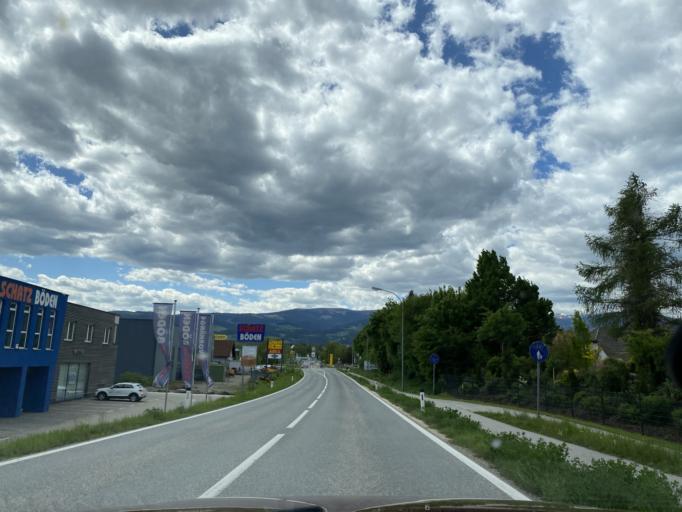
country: AT
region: Carinthia
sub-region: Politischer Bezirk Wolfsberg
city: Wolfsberg
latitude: 46.8186
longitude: 14.8455
